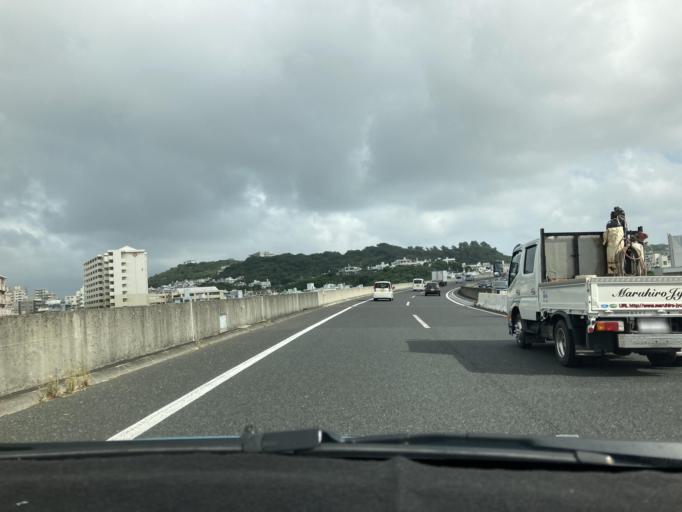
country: JP
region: Okinawa
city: Tomigusuku
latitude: 26.1753
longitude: 127.6738
